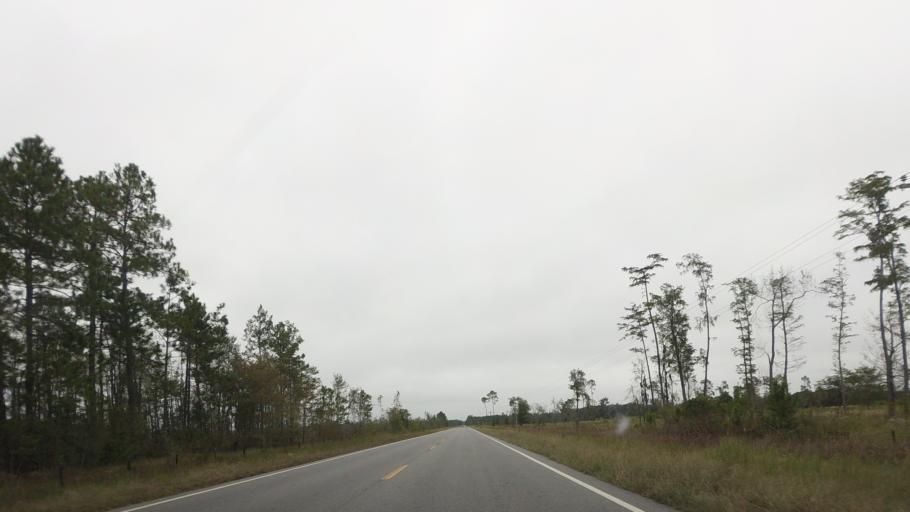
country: US
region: Georgia
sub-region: Berrien County
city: Enigma
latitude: 31.3544
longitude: -83.2278
